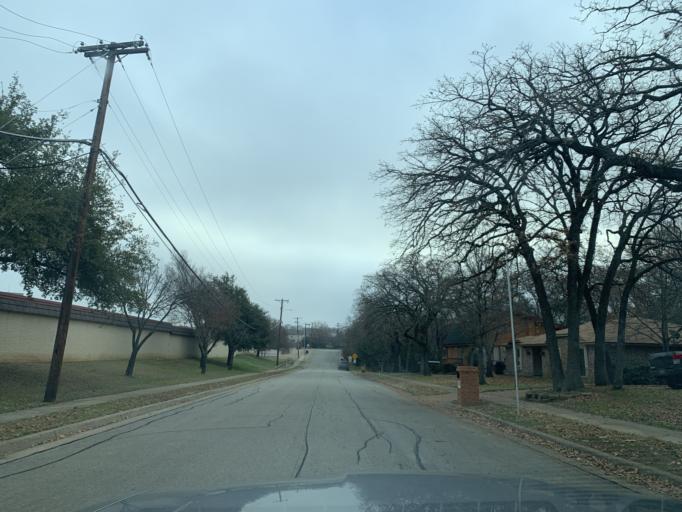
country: US
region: Texas
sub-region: Tarrant County
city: Bedford
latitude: 32.8344
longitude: -97.1447
